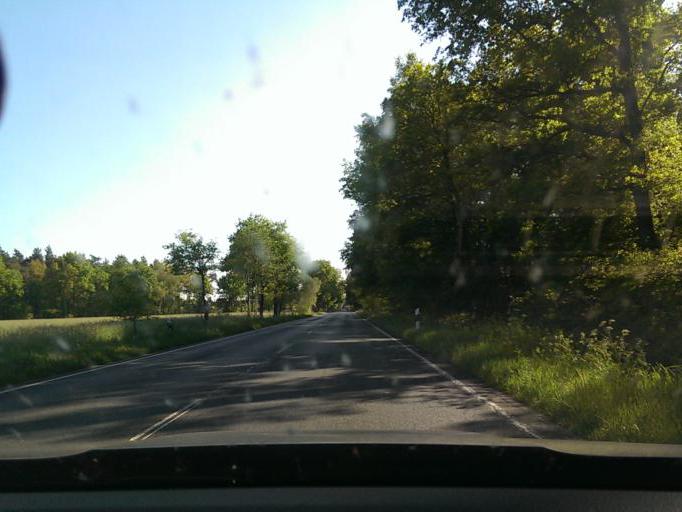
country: DE
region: Lower Saxony
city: Wietze
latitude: 52.5737
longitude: 9.8622
